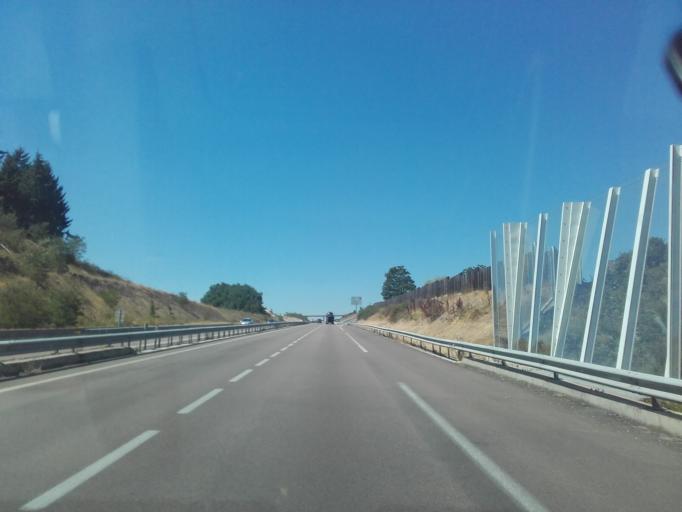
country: FR
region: Bourgogne
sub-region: Departement de Saone-et-Loire
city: Buxy
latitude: 46.7542
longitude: 4.6786
